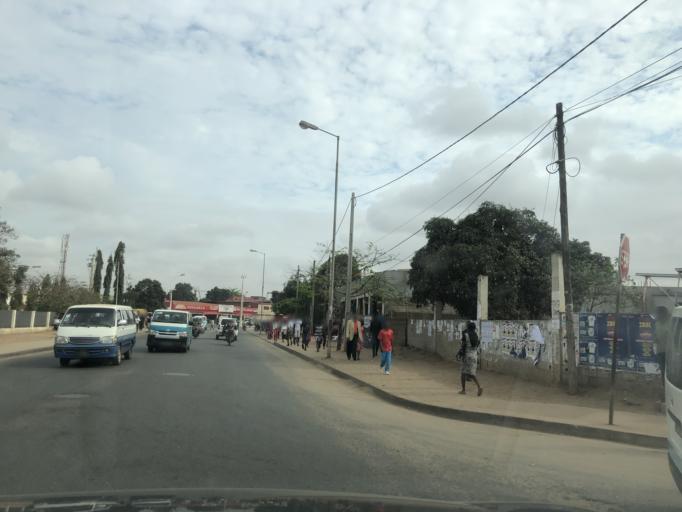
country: AO
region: Luanda
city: Luanda
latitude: -8.9127
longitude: 13.3717
